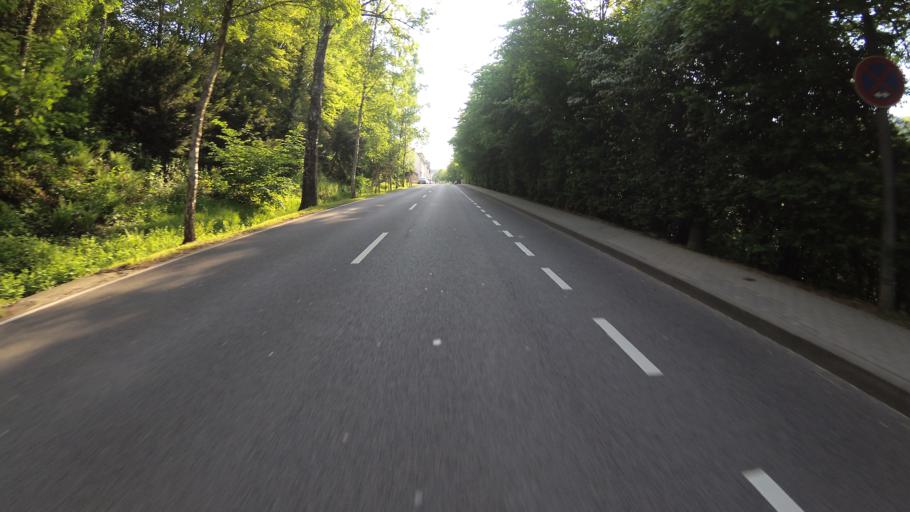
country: DE
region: Rheinland-Pfalz
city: Pirmasens
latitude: 49.2057
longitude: 7.6134
